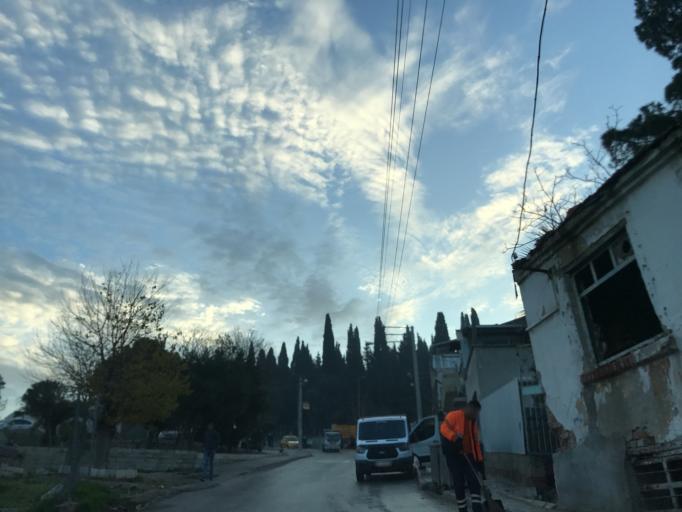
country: TR
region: Izmir
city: Izmir
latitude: 38.4128
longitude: 27.1398
